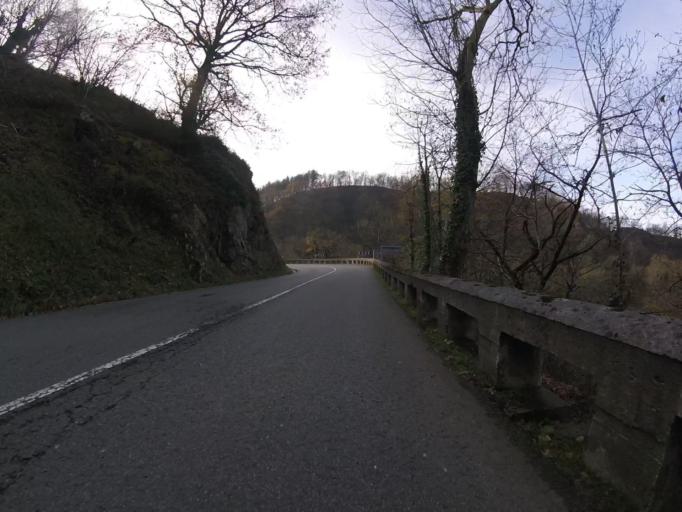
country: ES
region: Basque Country
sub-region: Provincia de Guipuzcoa
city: Elduayen
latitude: 43.1389
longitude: -1.9885
